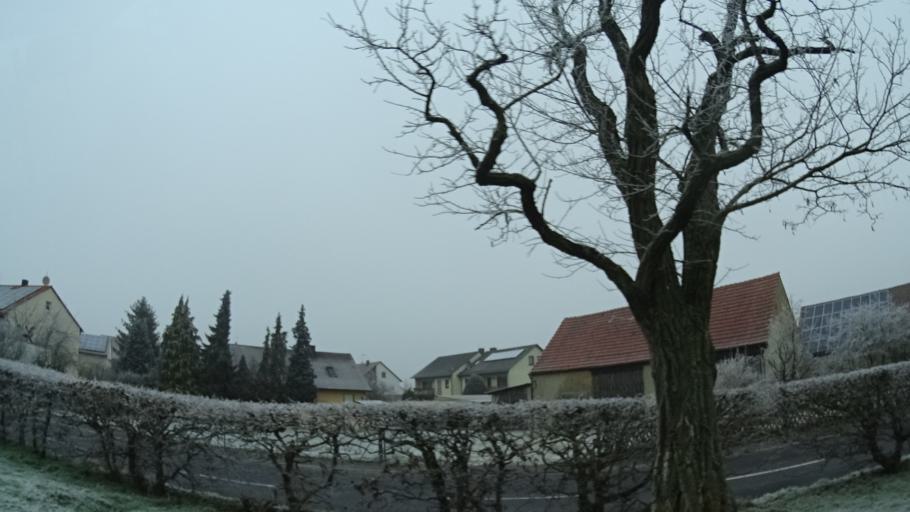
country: DE
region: Bavaria
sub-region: Regierungsbezirk Unterfranken
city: Lulsfeld
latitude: 49.8438
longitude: 10.2981
